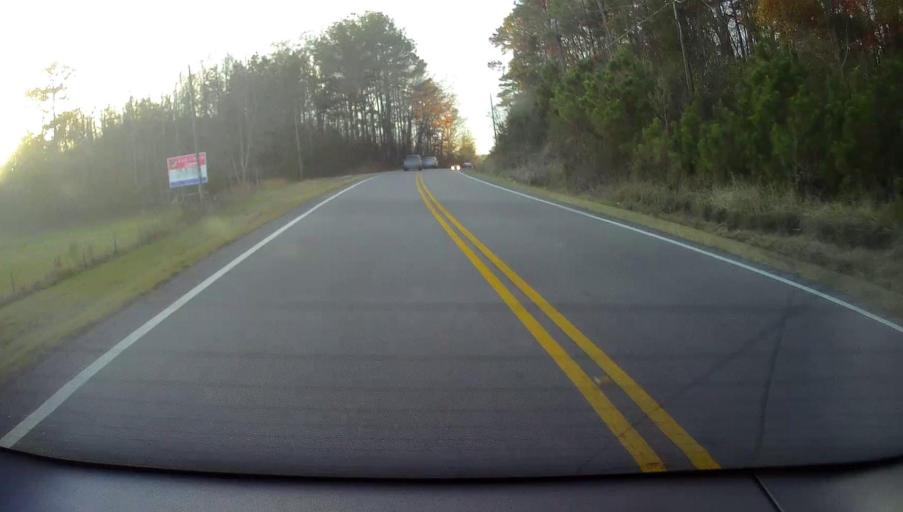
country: US
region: Alabama
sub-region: Saint Clair County
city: Steele
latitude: 34.0665
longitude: -86.2610
